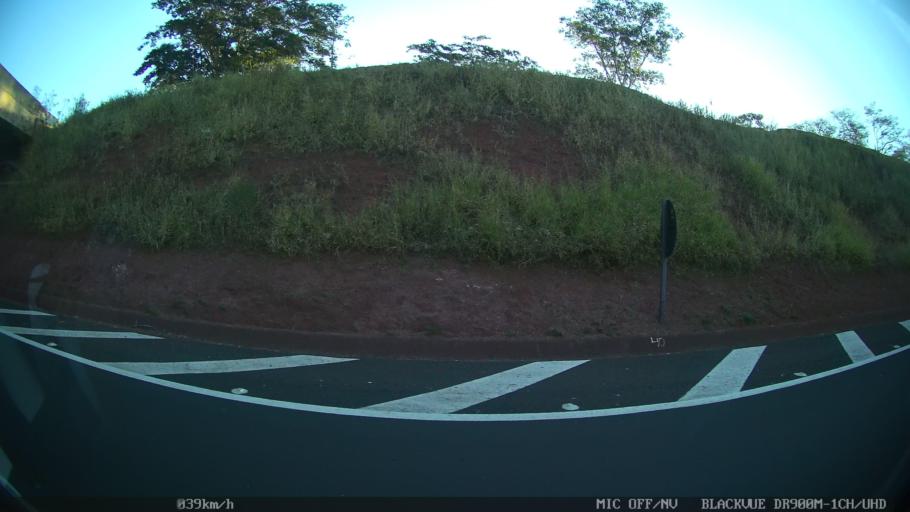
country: BR
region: Sao Paulo
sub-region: Araraquara
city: Araraquara
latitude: -21.8179
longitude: -48.2072
